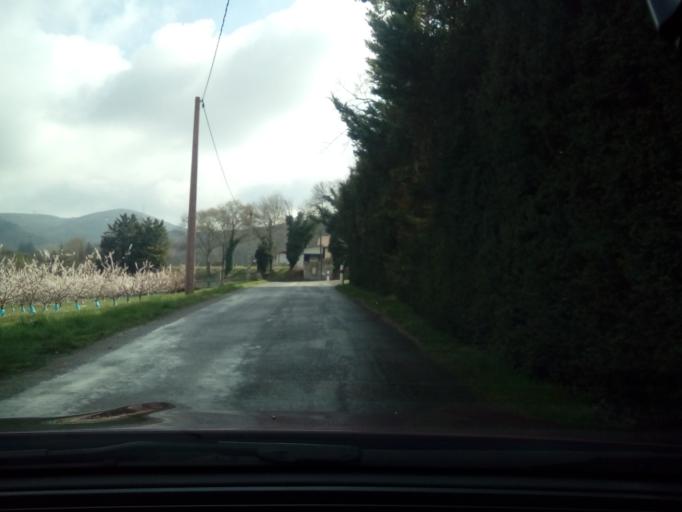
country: FR
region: Rhone-Alpes
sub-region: Departement de la Drome
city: Saulce-sur-Rhone
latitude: 44.7015
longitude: 4.8448
